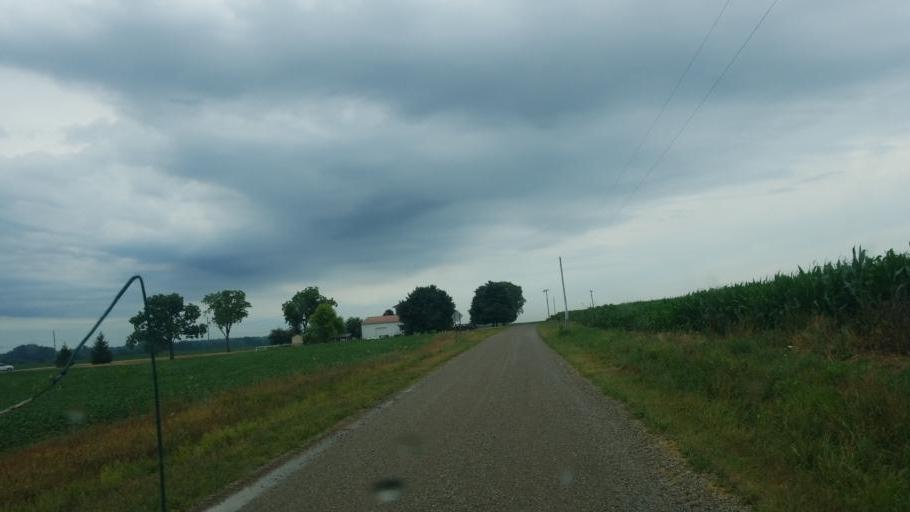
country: US
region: Indiana
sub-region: Steuben County
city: Hamilton
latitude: 41.4975
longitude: -84.9415
